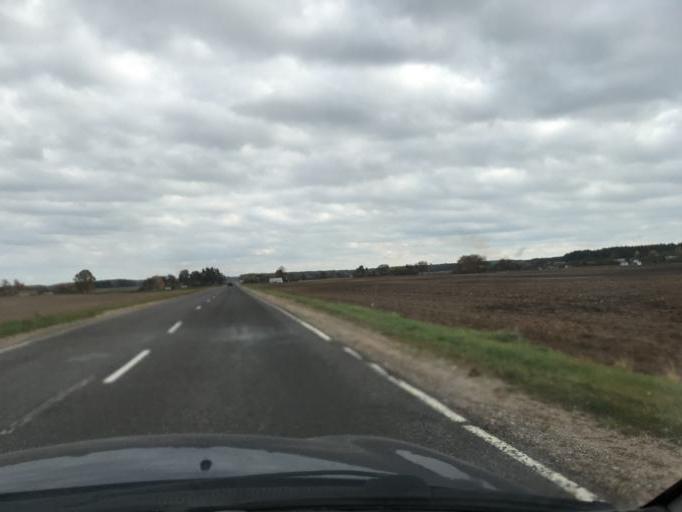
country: BY
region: Grodnenskaya
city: Lida
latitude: 53.7486
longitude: 25.2471
